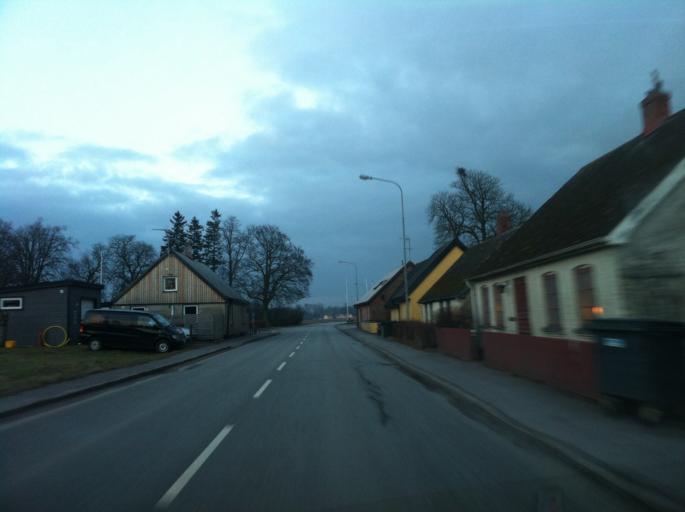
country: SE
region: Skane
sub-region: Svalovs Kommun
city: Teckomatorp
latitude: 55.8386
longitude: 13.0997
